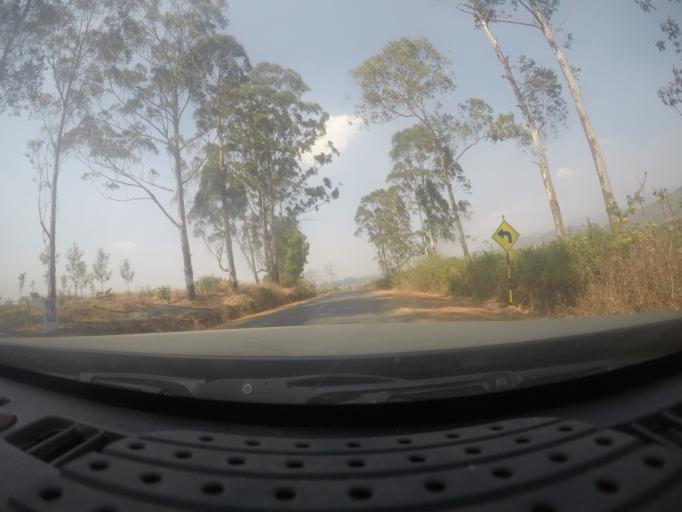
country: MM
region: Shan
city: Taunggyi
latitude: 21.0235
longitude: 96.5251
